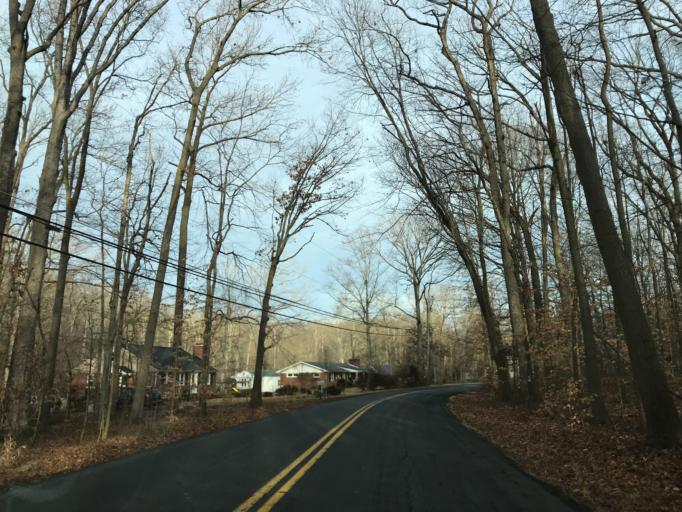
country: US
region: Maryland
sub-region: Harford County
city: Joppatowne
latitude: 39.4510
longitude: -76.3693
